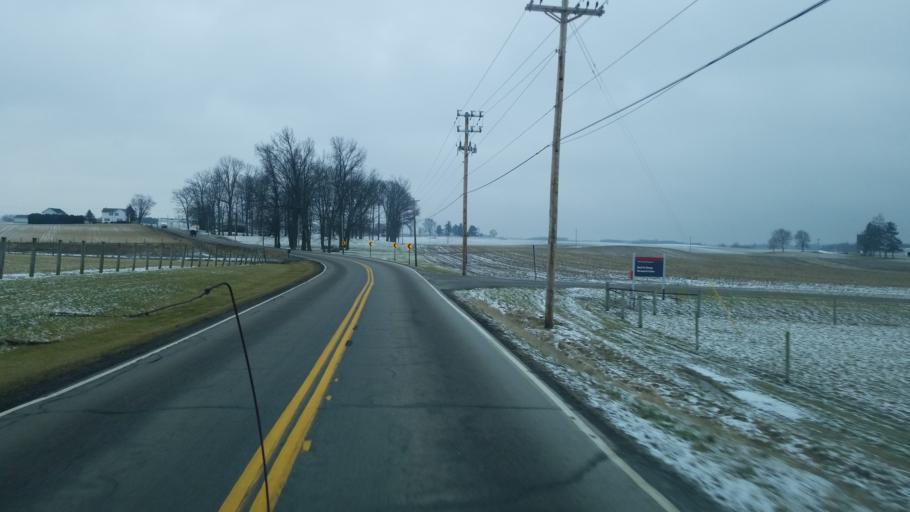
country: US
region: Ohio
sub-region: Wayne County
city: Apple Creek
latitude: 40.7296
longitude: -81.8962
